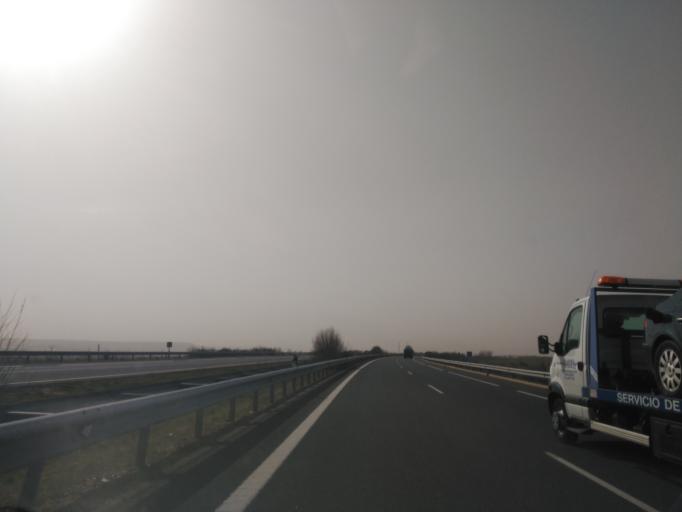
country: ES
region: Castille and Leon
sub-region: Provincia de Palencia
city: Pina de Campos
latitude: 42.2284
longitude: -4.4308
